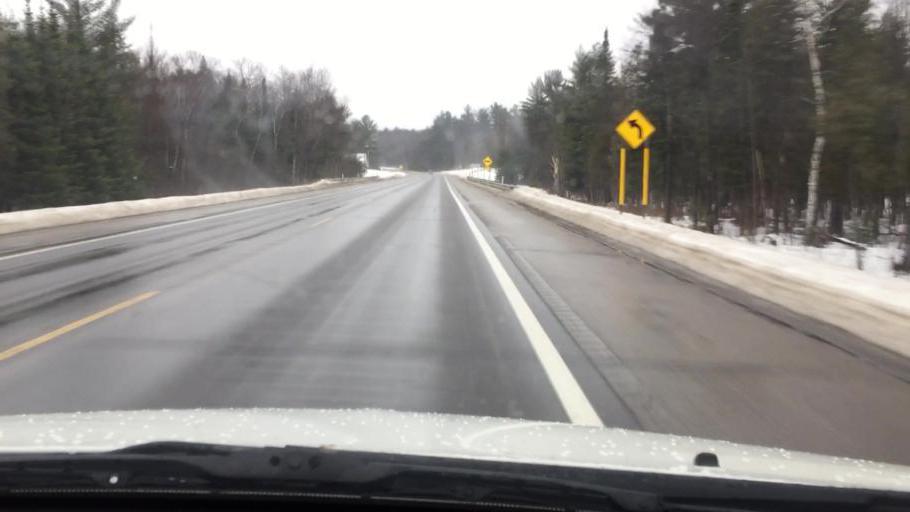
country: US
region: Michigan
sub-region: Kalkaska County
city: Kalkaska
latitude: 44.6463
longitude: -85.2776
